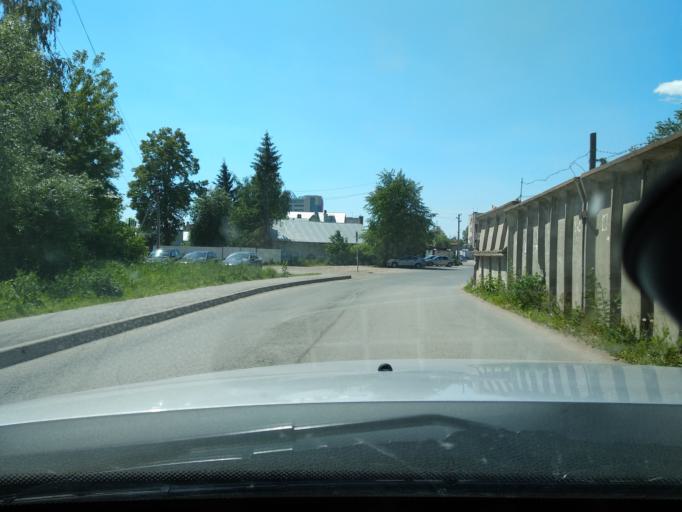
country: RU
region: Tatarstan
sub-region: Gorod Kazan'
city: Kazan
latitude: 55.8024
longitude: 49.2159
